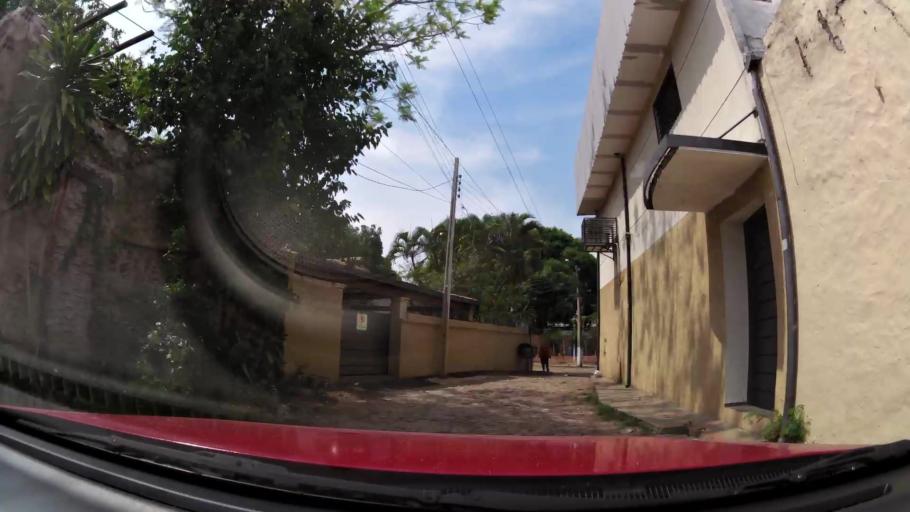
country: PY
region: Asuncion
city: Asuncion
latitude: -25.2639
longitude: -57.5873
